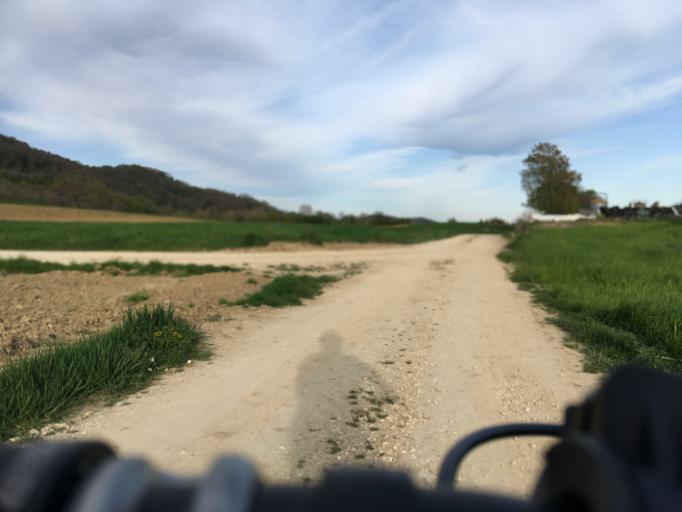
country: DE
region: Baden-Wuerttemberg
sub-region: Freiburg Region
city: Gottmadingen
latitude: 47.7394
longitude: 8.7592
